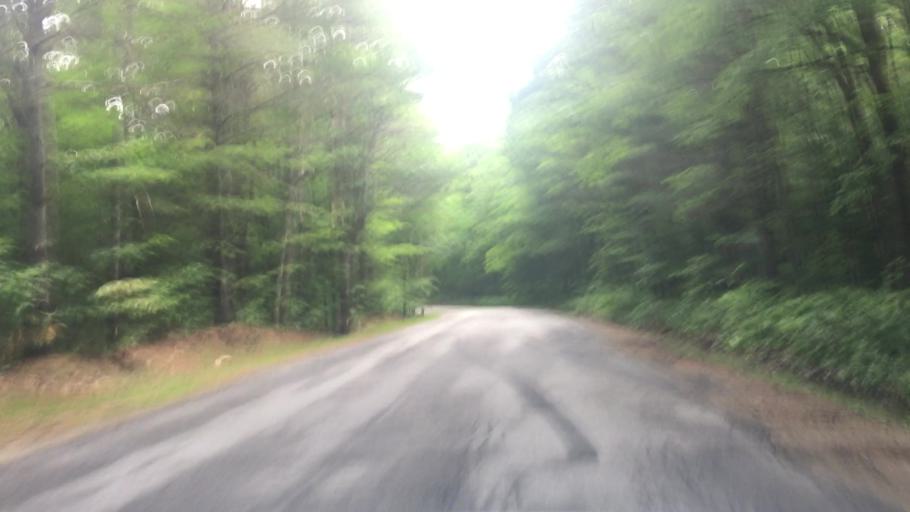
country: US
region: Maine
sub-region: Oxford County
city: South Paris
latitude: 44.2071
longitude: -70.5129
